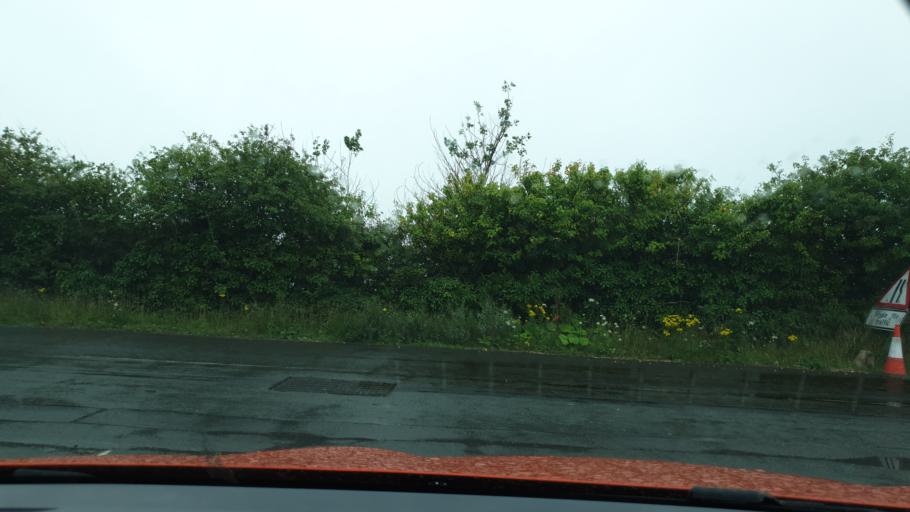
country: GB
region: England
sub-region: Cumbria
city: Barrow in Furness
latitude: 54.1201
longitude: -3.2555
